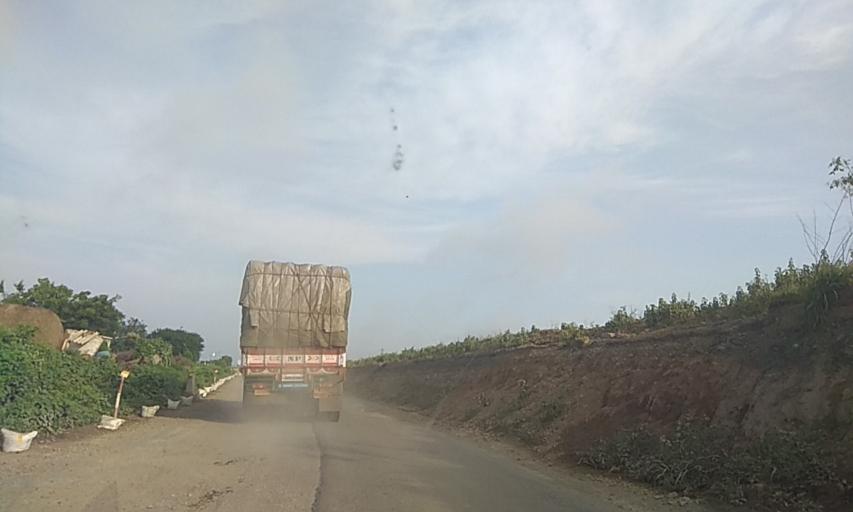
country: IN
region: Karnataka
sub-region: Haveri
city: Byadgi
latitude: 14.7205
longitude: 75.4800
